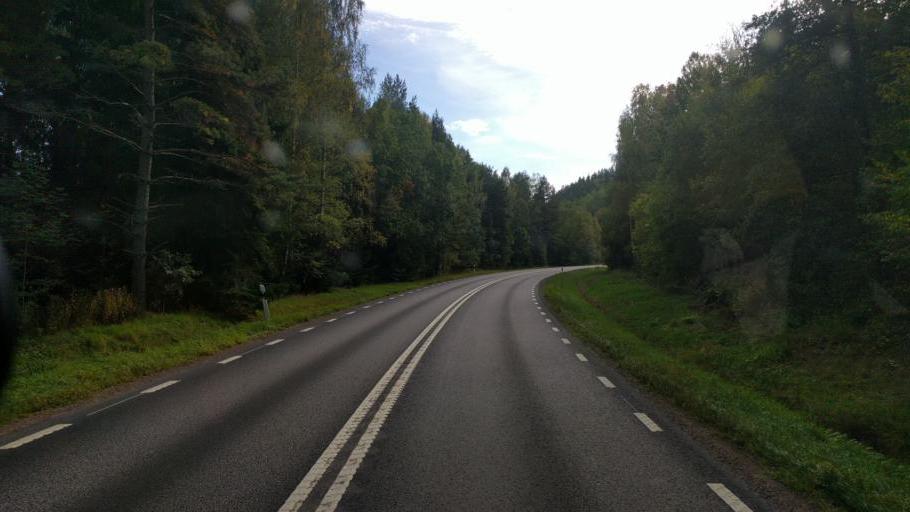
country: SE
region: OEstergoetland
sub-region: Kinda Kommun
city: Kisa
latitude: 57.9637
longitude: 15.6576
